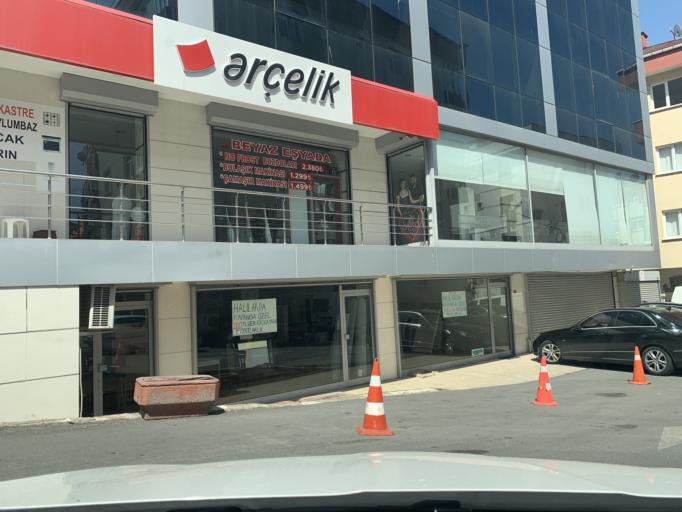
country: TR
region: Istanbul
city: Pendik
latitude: 40.8589
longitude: 29.2807
